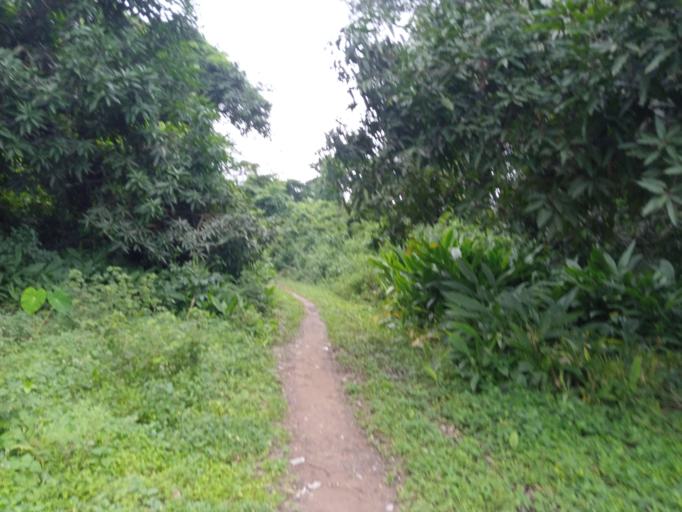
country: SL
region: Southern Province
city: Largo
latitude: 8.2086
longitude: -12.0570
